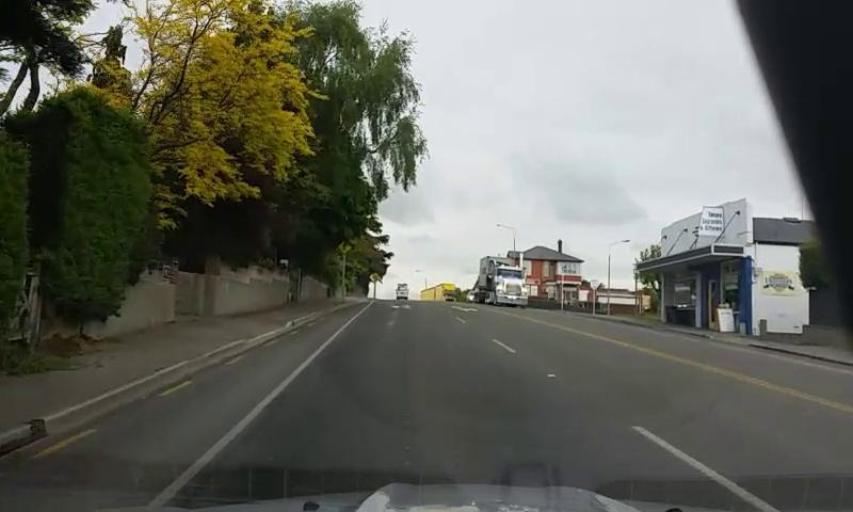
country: NZ
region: Canterbury
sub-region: Timaru District
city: Timaru
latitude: -44.3771
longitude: 171.2423
